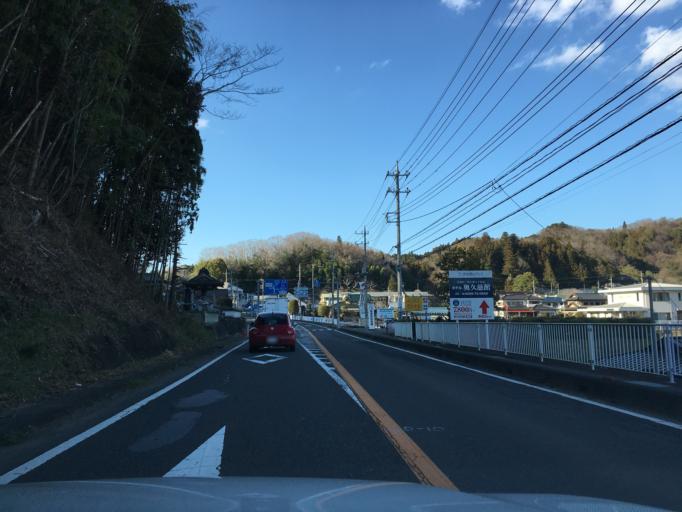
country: JP
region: Ibaraki
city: Daigo
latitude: 36.7564
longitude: 140.3827
